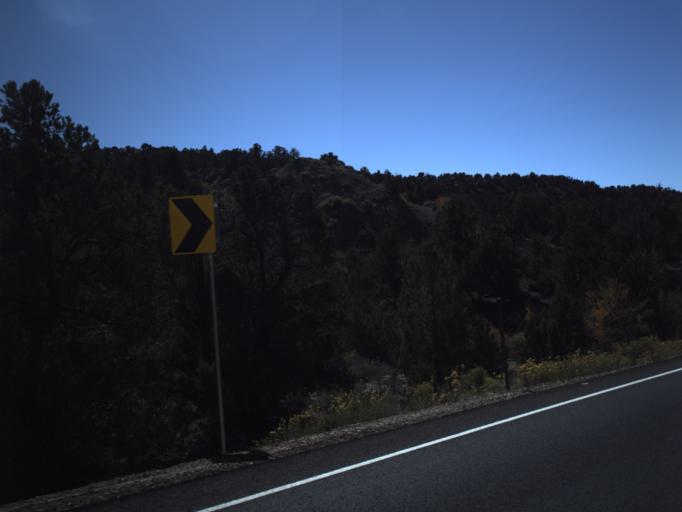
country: US
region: Utah
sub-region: Garfield County
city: Panguitch
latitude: 37.6236
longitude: -111.8537
